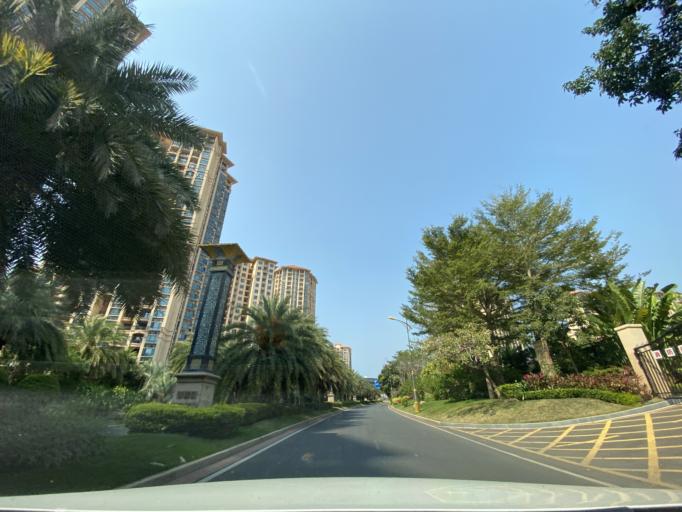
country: CN
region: Hainan
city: Yingzhou
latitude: 18.3953
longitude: 109.8405
